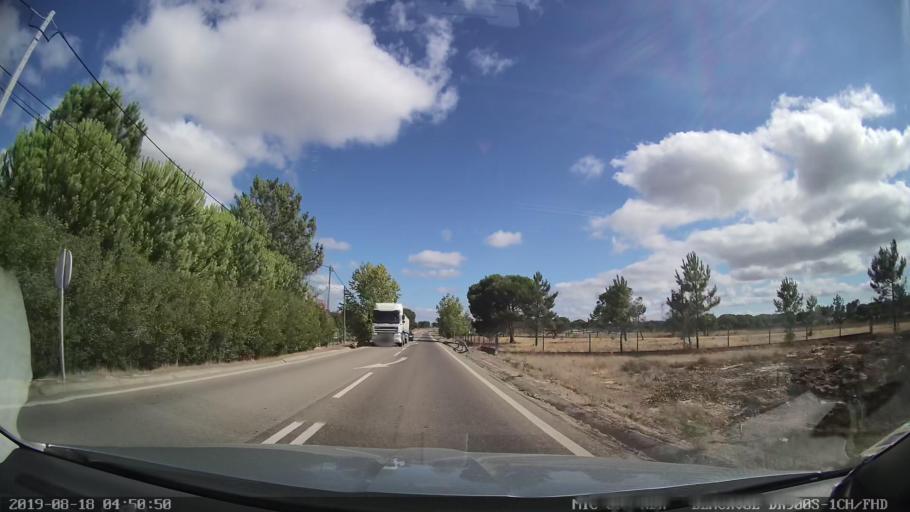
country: PT
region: Santarem
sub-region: Benavente
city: Benavente
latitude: 38.9312
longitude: -8.7793
